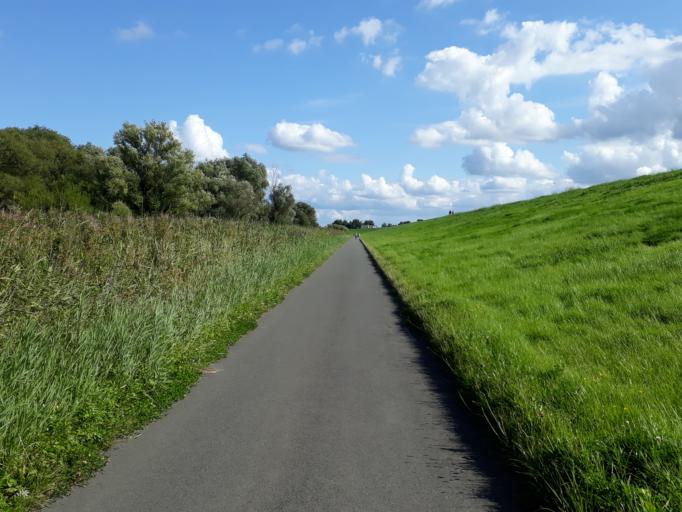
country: DE
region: Lower Saxony
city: Jork
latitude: 53.5579
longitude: 9.6615
